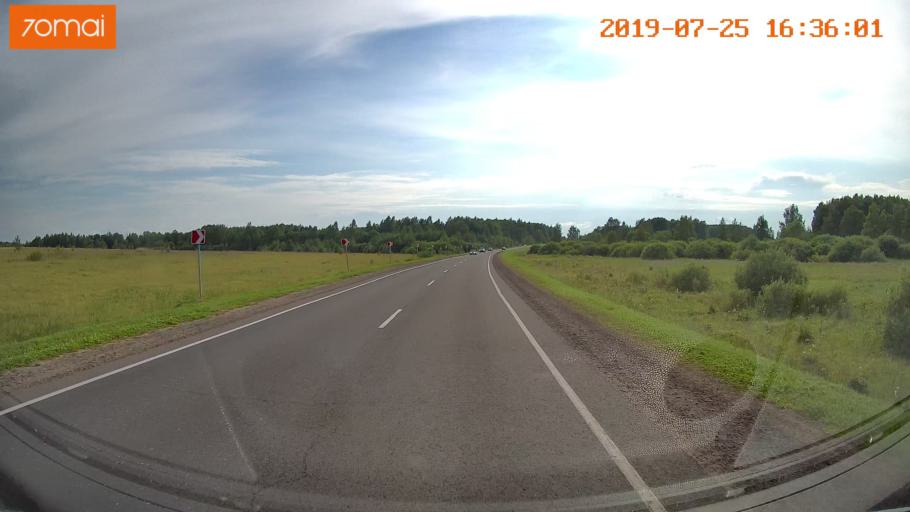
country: RU
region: Ivanovo
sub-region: Privolzhskiy Rayon
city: Ples
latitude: 57.3993
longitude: 41.4123
